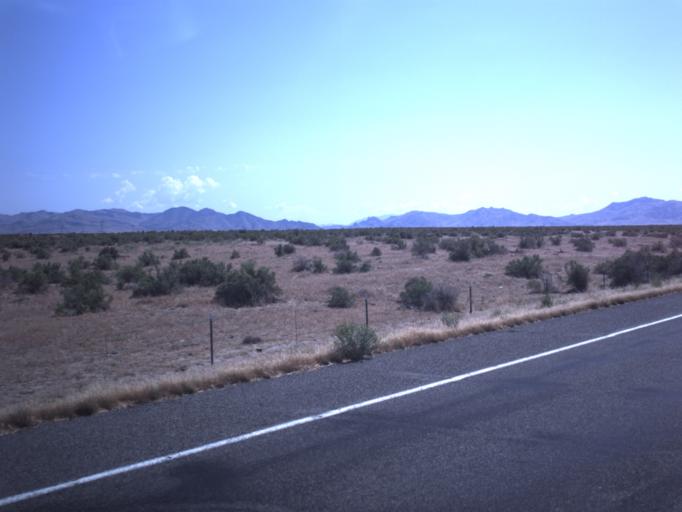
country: US
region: Utah
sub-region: Millard County
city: Delta
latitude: 39.4731
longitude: -112.4745
